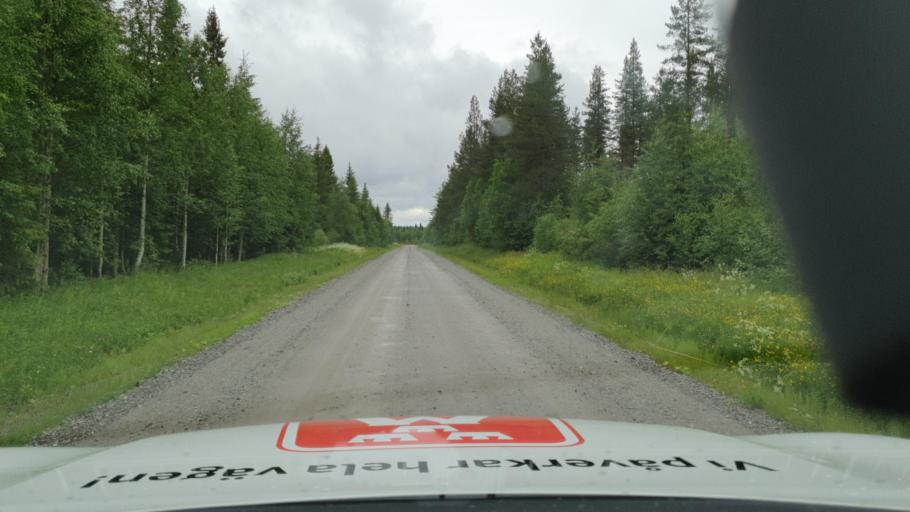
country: SE
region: Vaesterbotten
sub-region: Dorotea Kommun
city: Dorotea
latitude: 64.0850
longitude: 16.6805
